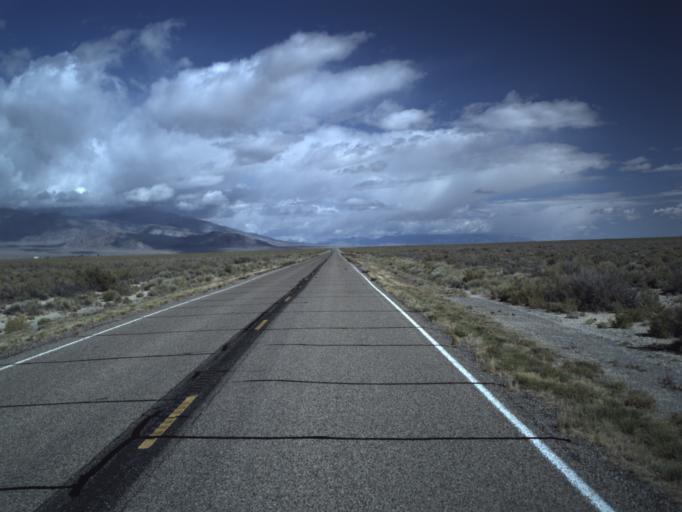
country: US
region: Nevada
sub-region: White Pine County
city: McGill
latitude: 39.0215
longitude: -114.0354
